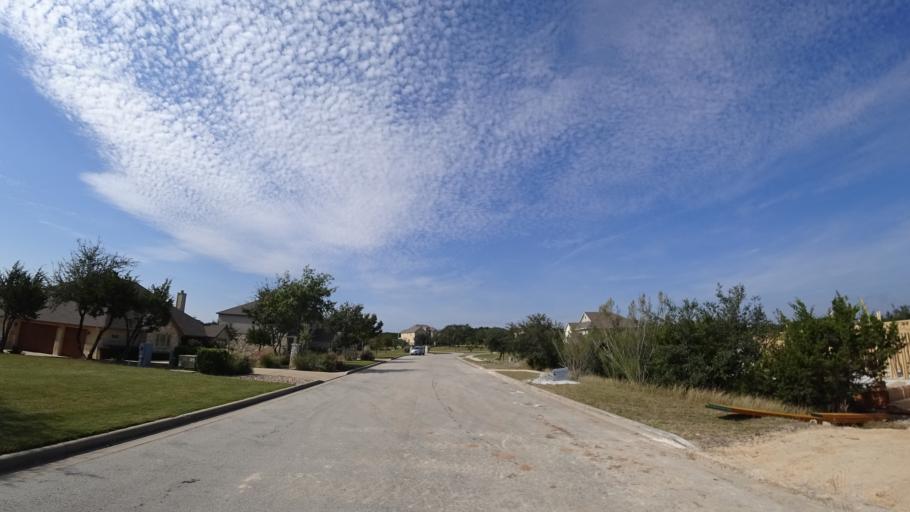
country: US
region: Texas
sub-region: Travis County
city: Bee Cave
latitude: 30.2260
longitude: -97.9319
